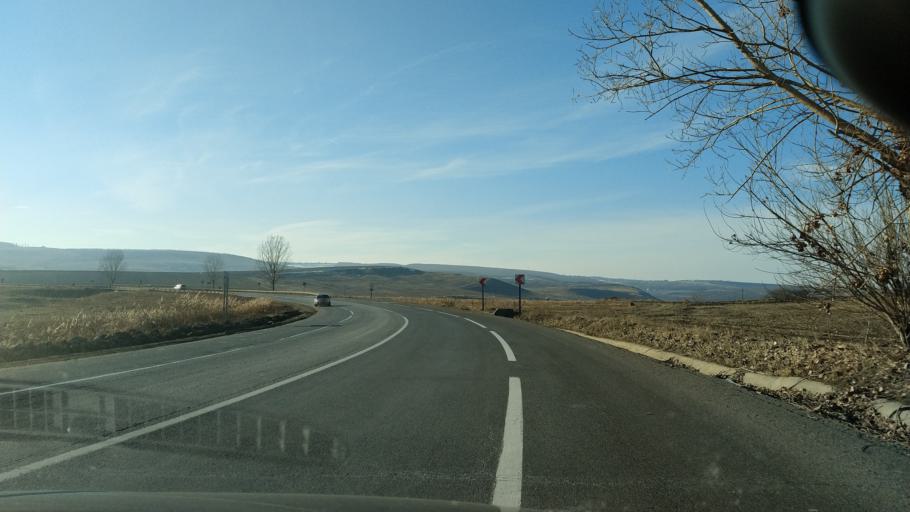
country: RO
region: Iasi
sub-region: Comuna Targu Frumos
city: Targu Frumos
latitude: 47.1982
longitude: 26.9772
